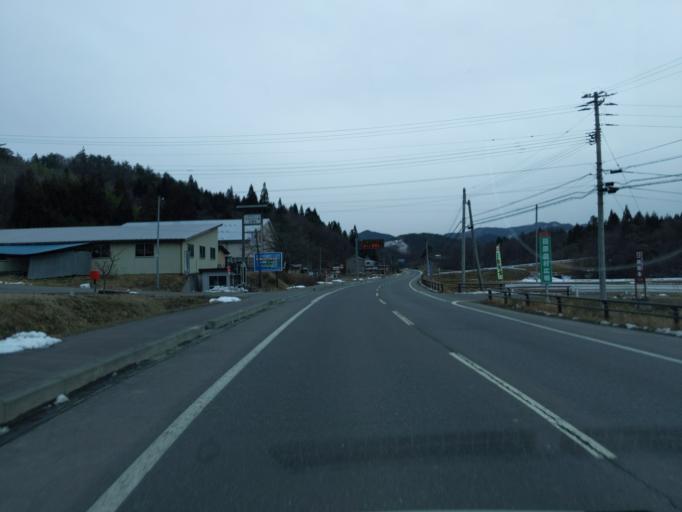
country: JP
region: Iwate
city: Mizusawa
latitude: 39.1546
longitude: 141.2276
